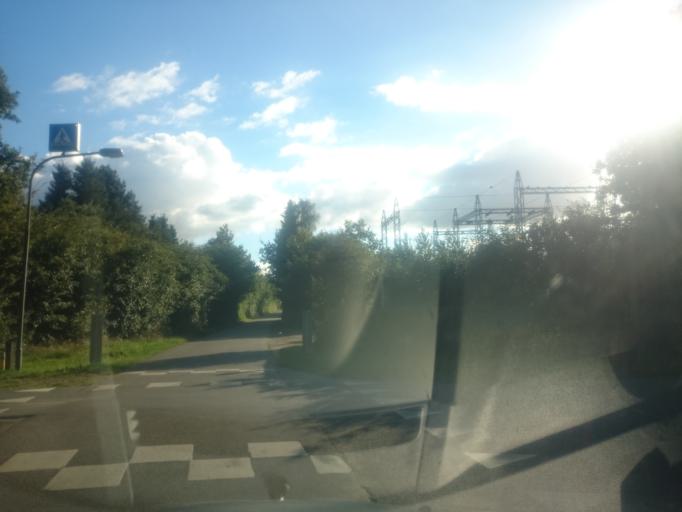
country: DK
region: South Denmark
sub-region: Billund Kommune
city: Billund
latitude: 55.7207
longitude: 9.1130
